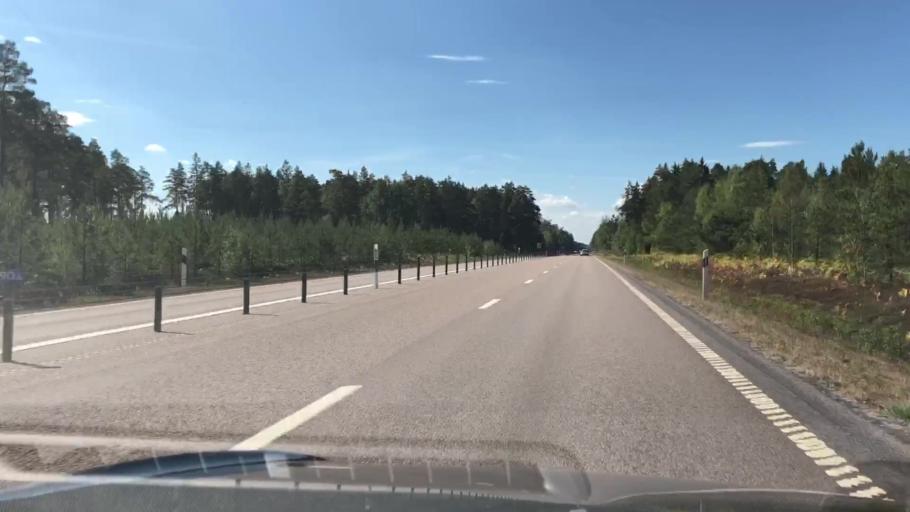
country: SE
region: Kalmar
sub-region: Monsteras Kommun
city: Moensteras
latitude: 57.0079
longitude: 16.4213
